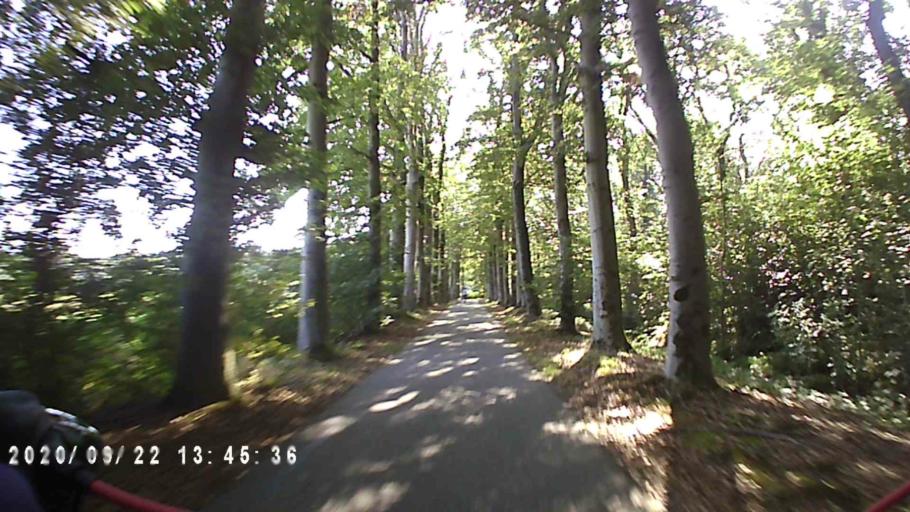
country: NL
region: Groningen
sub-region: Gemeente Leek
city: Leek
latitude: 53.1459
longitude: 6.4075
